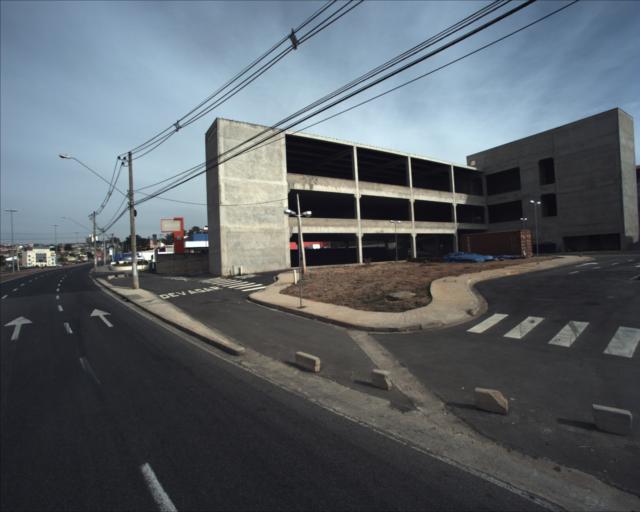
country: BR
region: Sao Paulo
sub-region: Sorocaba
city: Sorocaba
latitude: -23.4809
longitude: -47.4583
